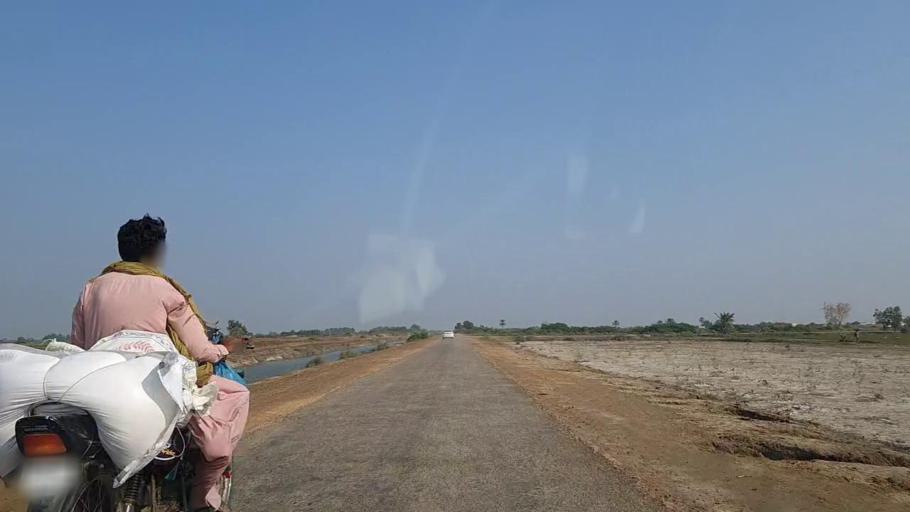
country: PK
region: Sindh
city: Mirpur Sakro
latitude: 24.6344
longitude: 67.6127
